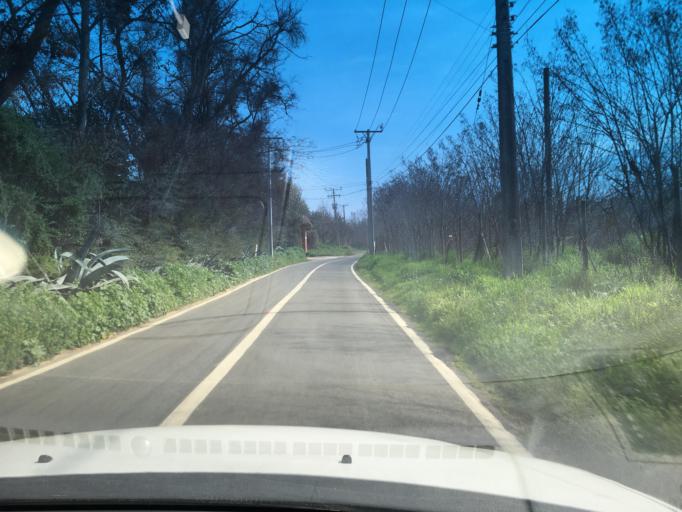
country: CL
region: Valparaiso
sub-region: Provincia de Marga Marga
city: Limache
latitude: -33.0073
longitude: -71.2221
